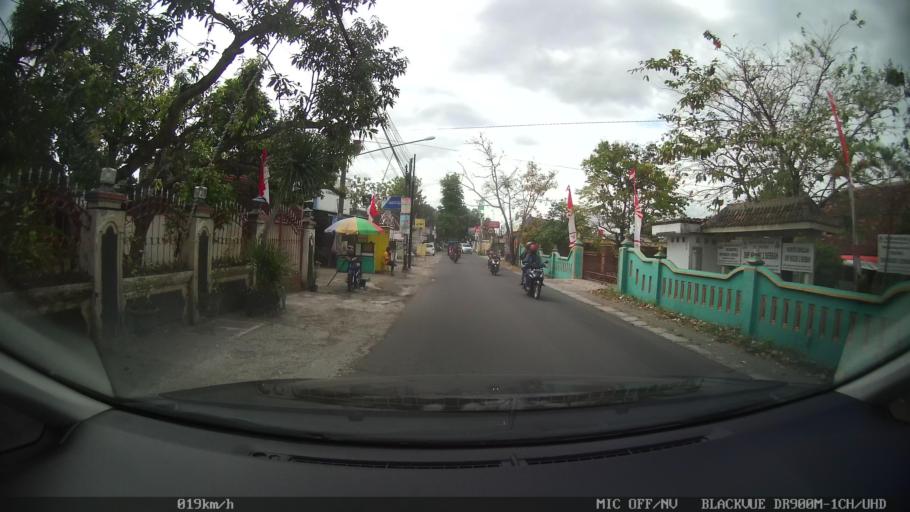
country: ID
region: Daerah Istimewa Yogyakarta
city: Depok
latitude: -7.8051
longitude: 110.4445
